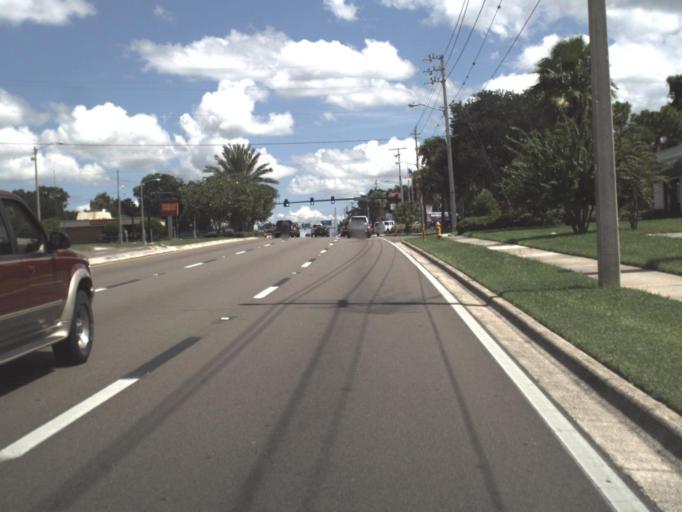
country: US
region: Florida
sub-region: Polk County
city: Winter Haven
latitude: 28.0440
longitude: -81.7399
